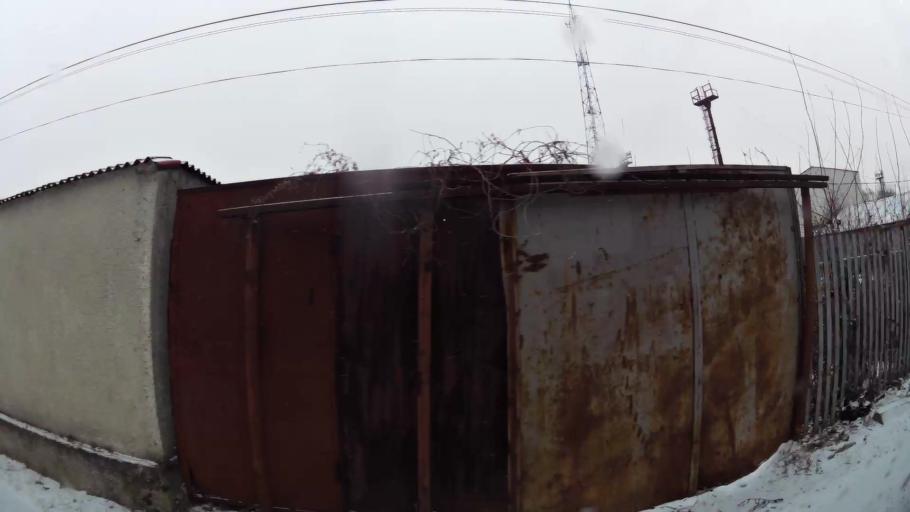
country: RO
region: Dambovita
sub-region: Municipiul Targoviste
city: Targoviste
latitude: 44.9164
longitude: 25.4644
